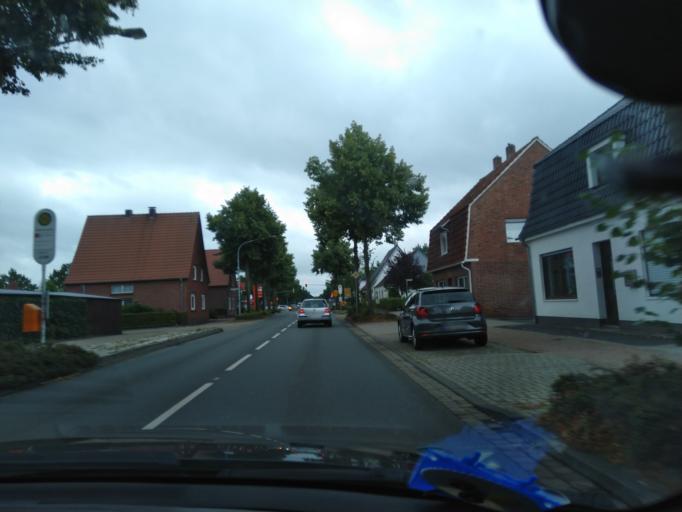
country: DE
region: Lower Saxony
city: Nordhorn
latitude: 52.4204
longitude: 7.0829
